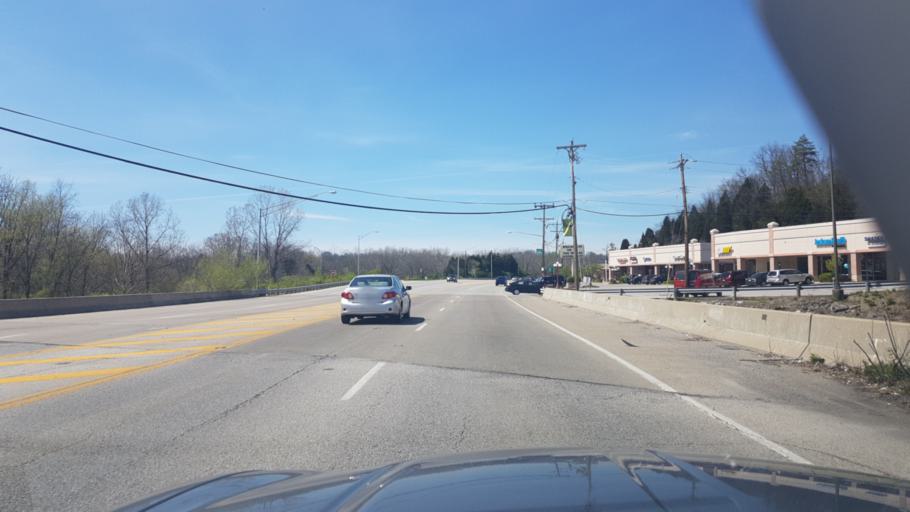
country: US
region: Ohio
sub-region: Hamilton County
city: Turpin Hills
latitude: 39.1063
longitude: -84.3966
